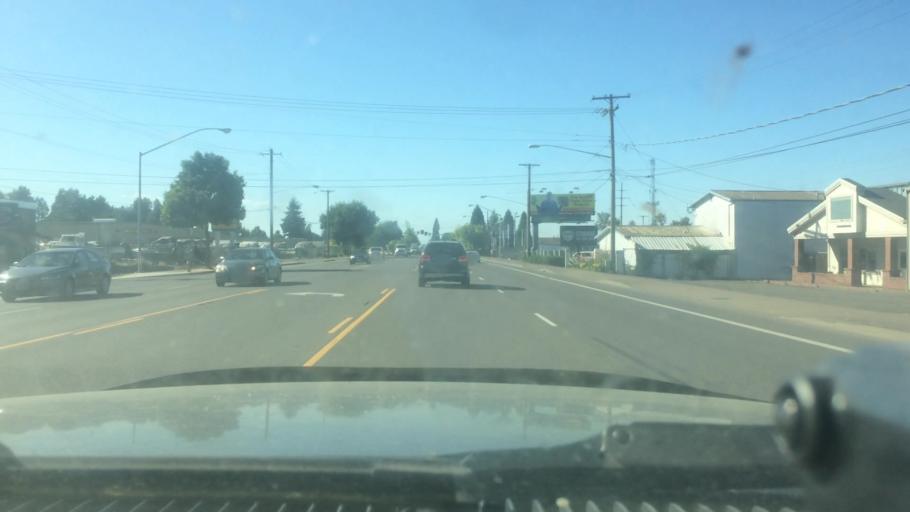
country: US
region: Oregon
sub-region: Lane County
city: Eugene
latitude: 44.0783
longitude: -123.1500
